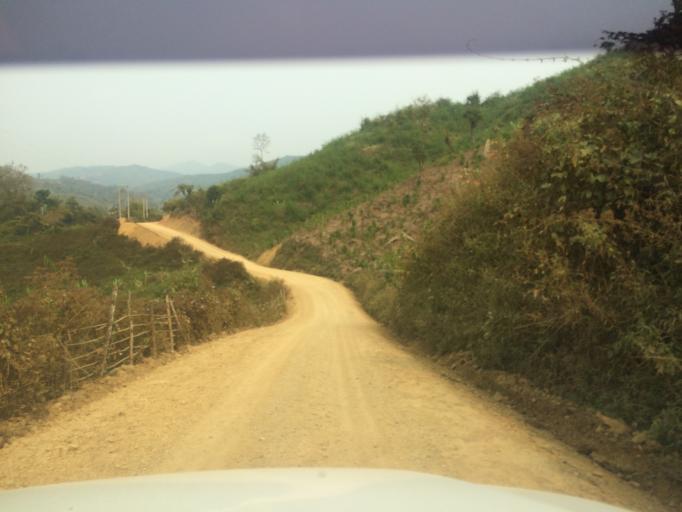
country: LA
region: Loungnamtha
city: Muang Nale
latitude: 20.4375
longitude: 101.7156
